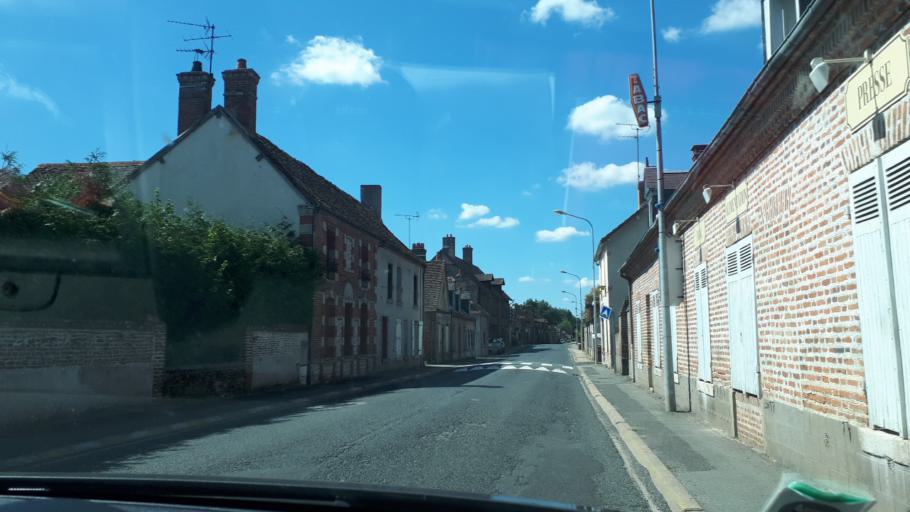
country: FR
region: Centre
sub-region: Departement du Loir-et-Cher
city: Neung-sur-Beuvron
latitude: 47.5425
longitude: 1.8491
